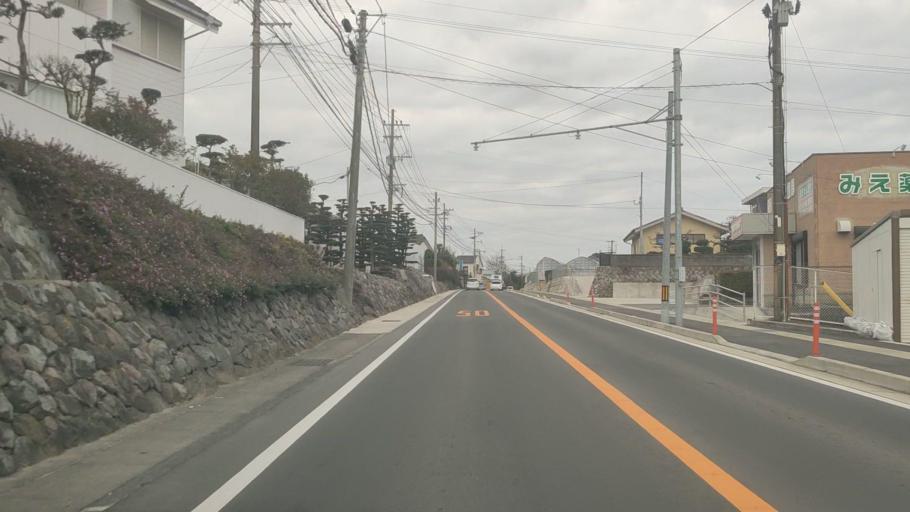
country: JP
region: Nagasaki
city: Shimabara
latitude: 32.8158
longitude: 130.3561
